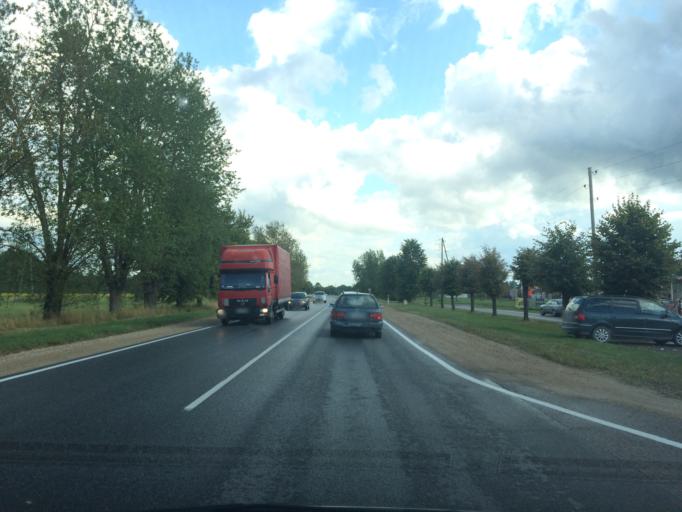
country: LV
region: Ogre
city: Ogre
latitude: 56.7784
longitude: 24.6545
